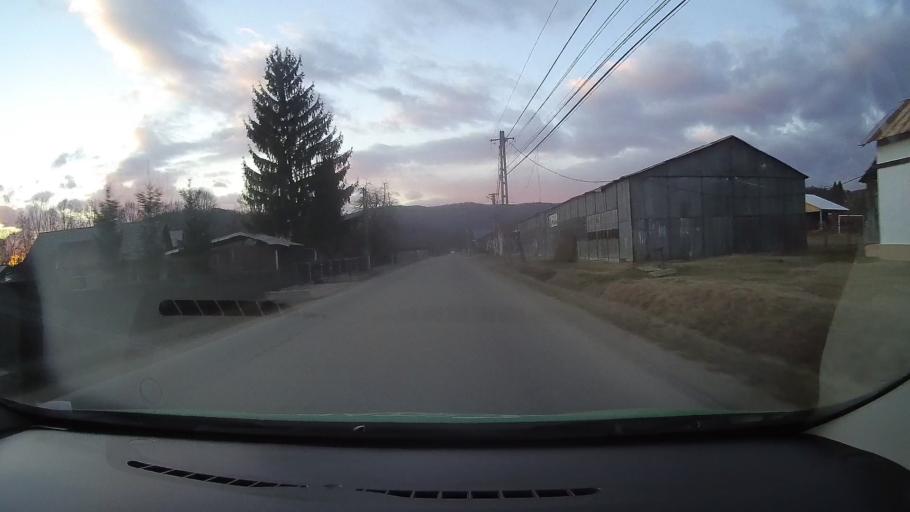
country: RO
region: Dambovita
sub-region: Comuna Valea Lunga
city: Valea Lunga-Cricov
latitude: 45.0667
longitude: 25.5838
